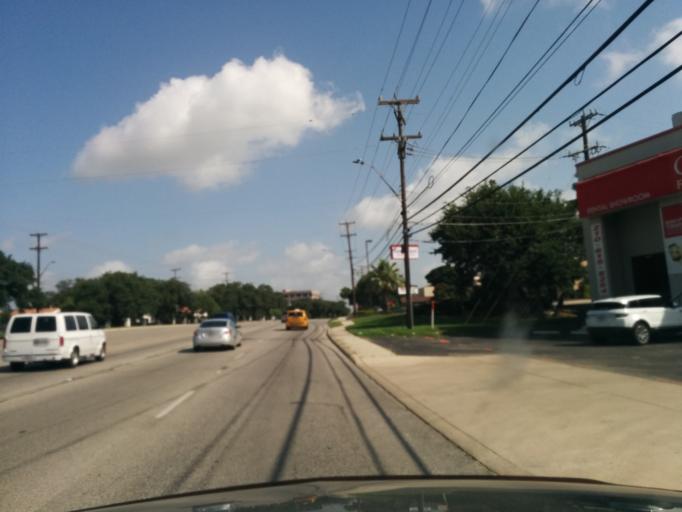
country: US
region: Texas
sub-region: Bexar County
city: Balcones Heights
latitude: 29.5154
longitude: -98.5713
